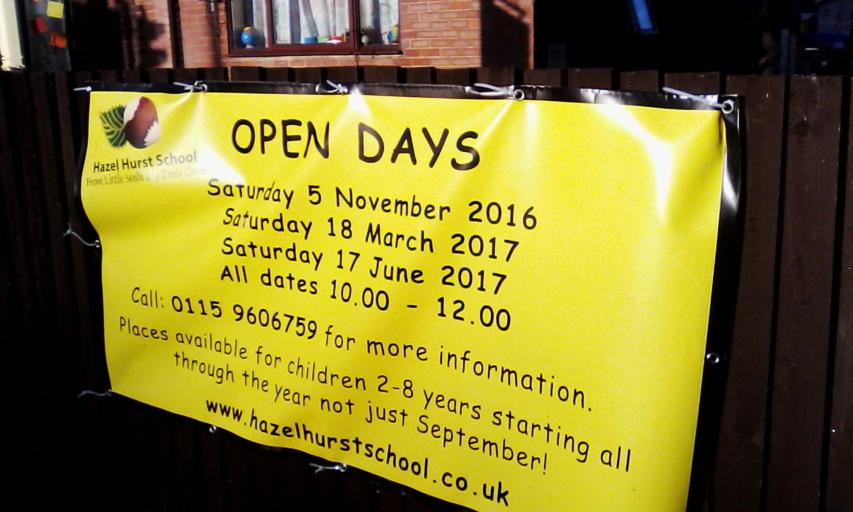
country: GB
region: England
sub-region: Nottinghamshire
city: Arnold
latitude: 52.9841
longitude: -1.1144
